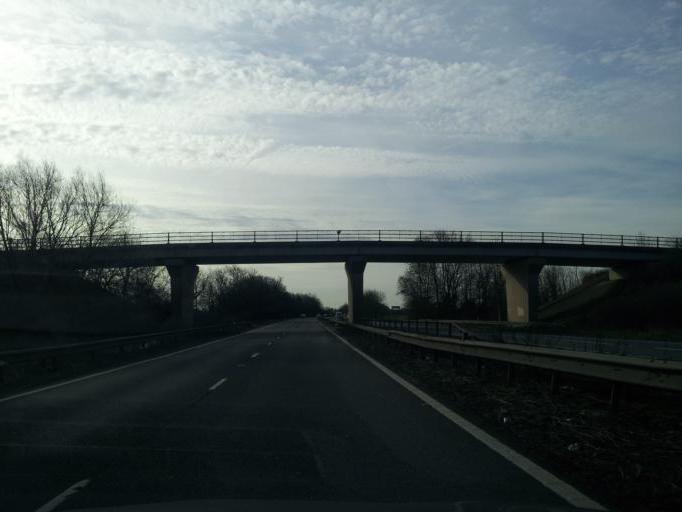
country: GB
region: England
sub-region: Cambridgeshire
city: Buckden
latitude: 52.3152
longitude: -0.2438
